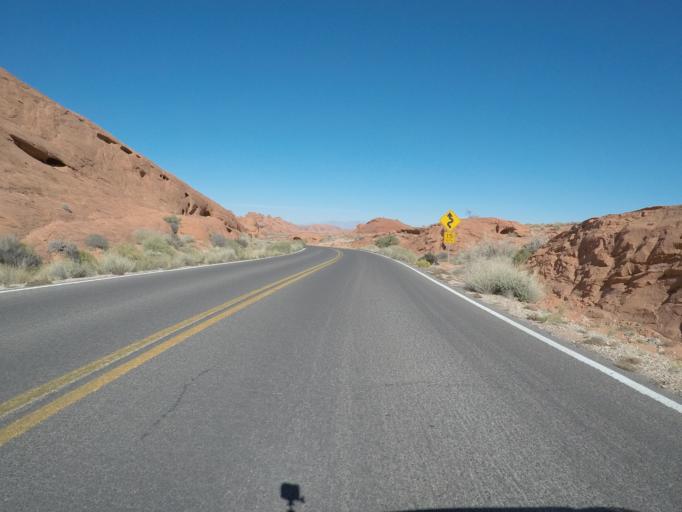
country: US
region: Nevada
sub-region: Clark County
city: Moapa Valley
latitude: 36.4885
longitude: -114.5333
